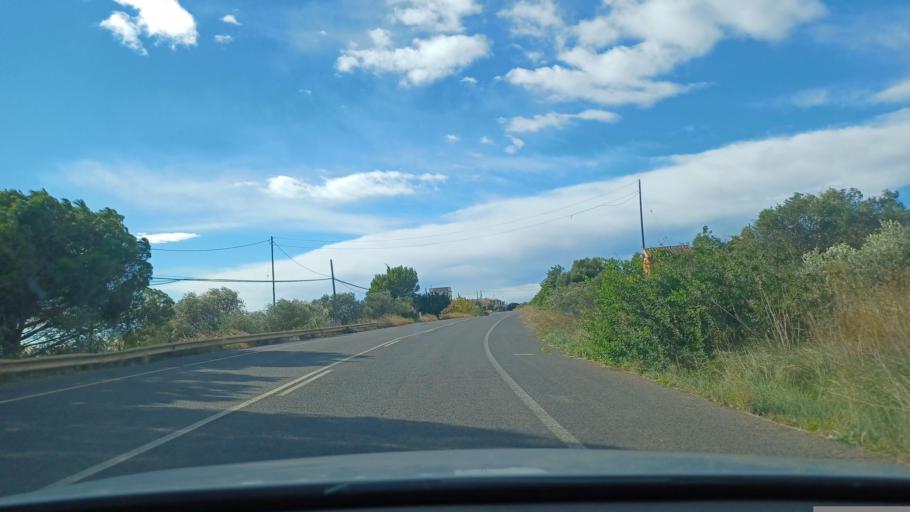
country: ES
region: Catalonia
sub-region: Provincia de Tarragona
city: Sant Carles de la Rapita
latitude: 40.5812
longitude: 0.5548
